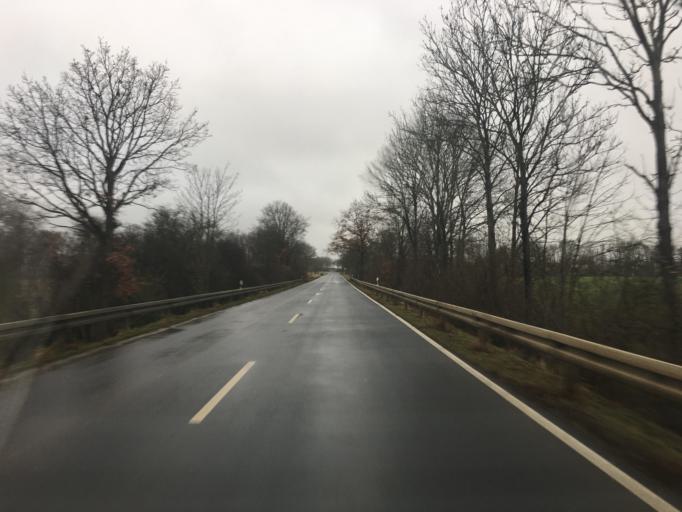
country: DE
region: North Rhine-Westphalia
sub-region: Regierungsbezirk Koln
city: Rheinbach
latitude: 50.6443
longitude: 6.9321
